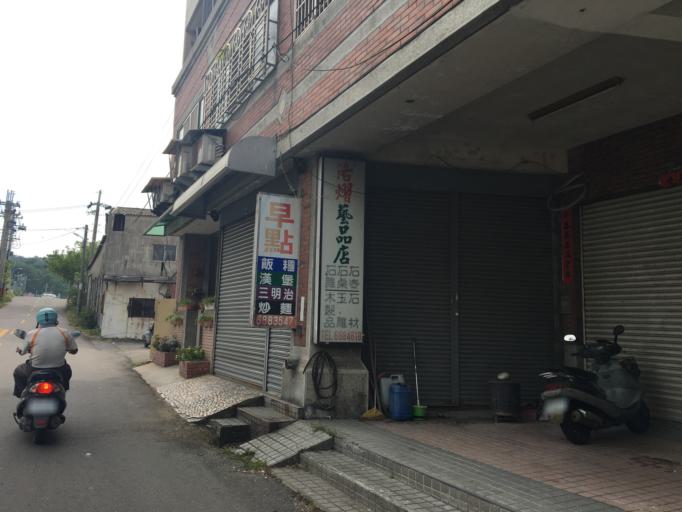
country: TW
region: Taiwan
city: Fengyuan
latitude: 24.3400
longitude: 120.6249
